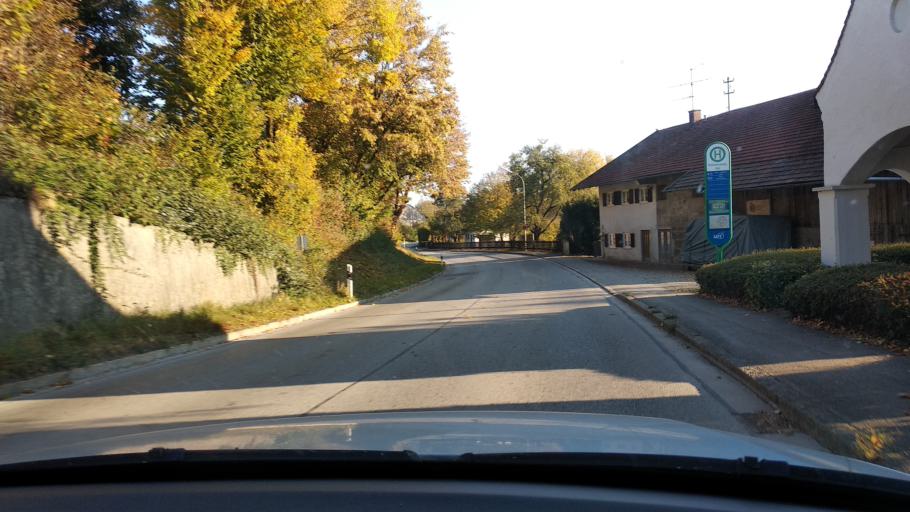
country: DE
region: Bavaria
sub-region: Upper Bavaria
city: Oberpframmern
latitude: 47.9953
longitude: 11.8295
